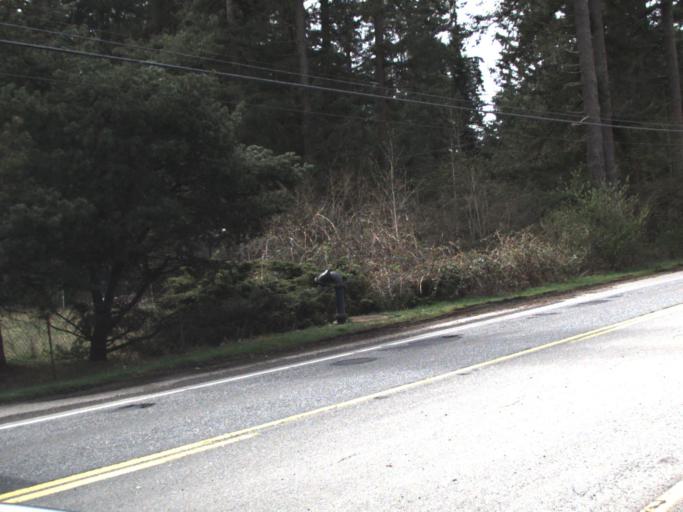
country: US
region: Washington
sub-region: King County
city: Lake Morton-Berrydale
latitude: 47.3581
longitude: -122.0849
